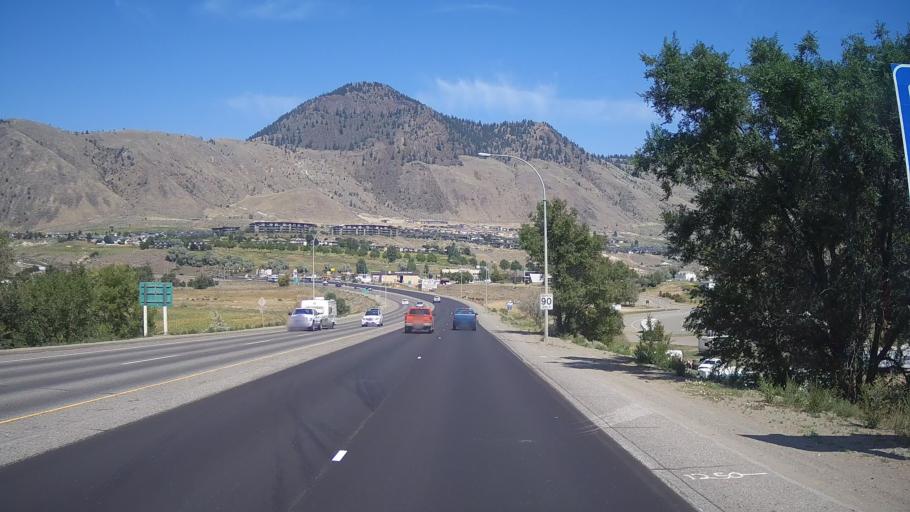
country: CA
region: British Columbia
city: Kamloops
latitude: 50.6793
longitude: -120.3030
